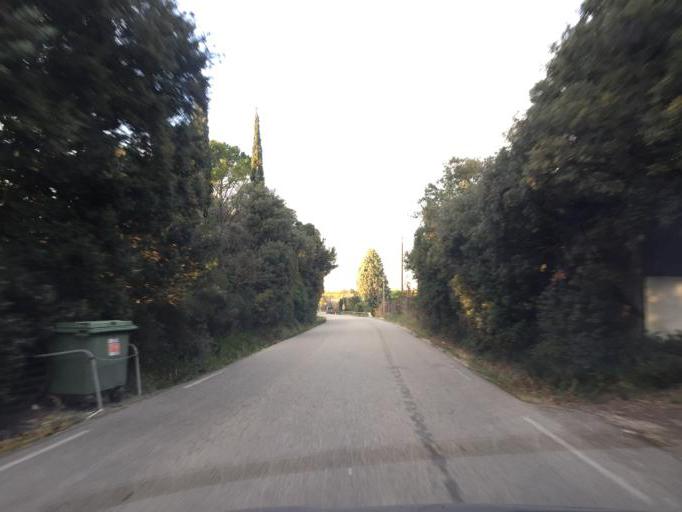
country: FR
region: Provence-Alpes-Cote d'Azur
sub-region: Departement du Vaucluse
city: Courthezon
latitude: 44.1078
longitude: 4.8759
